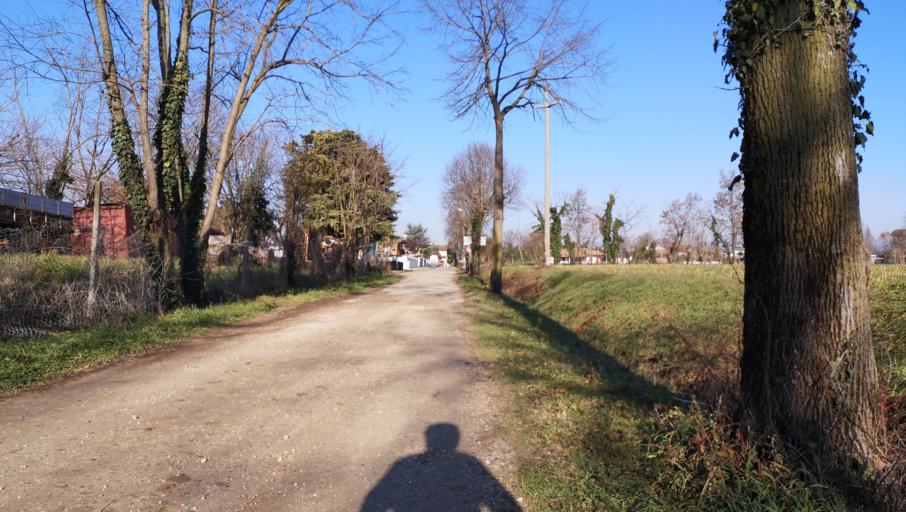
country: IT
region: Friuli Venezia Giulia
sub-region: Provincia di Udine
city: Santa Maria la Longa
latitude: 45.9187
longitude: 13.2979
